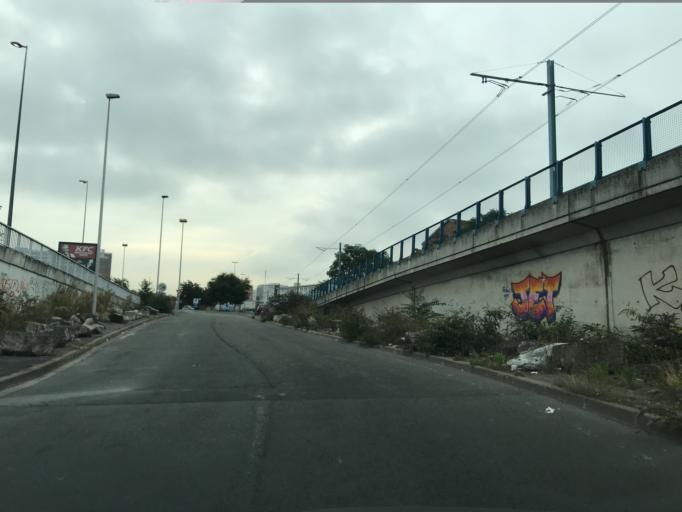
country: FR
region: Ile-de-France
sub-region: Departement de Seine-Saint-Denis
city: Drancy
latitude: 48.9148
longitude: 2.4297
